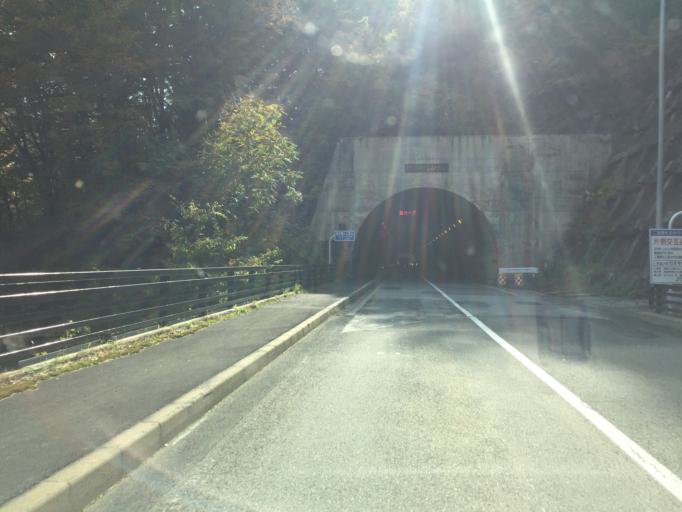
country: JP
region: Fukushima
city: Kitakata
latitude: 37.7845
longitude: 139.9320
